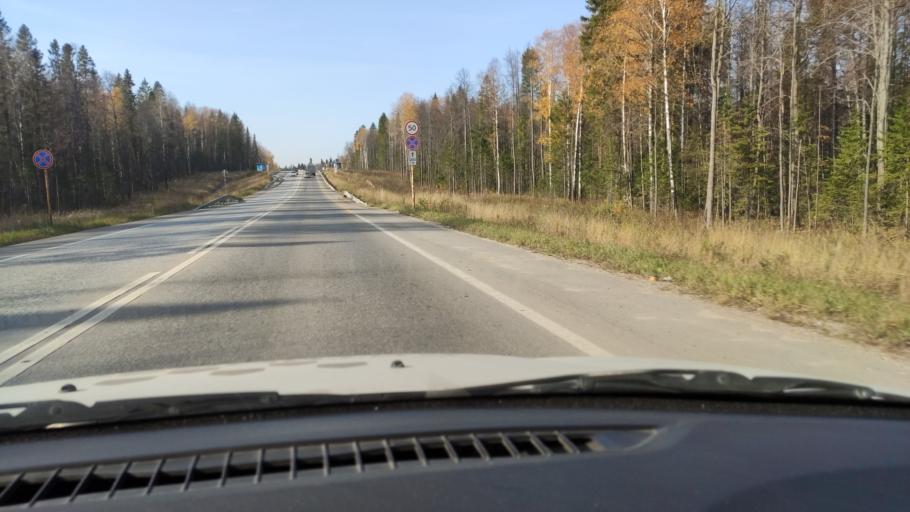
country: RU
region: Perm
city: Novyye Lyady
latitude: 58.0494
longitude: 56.5571
